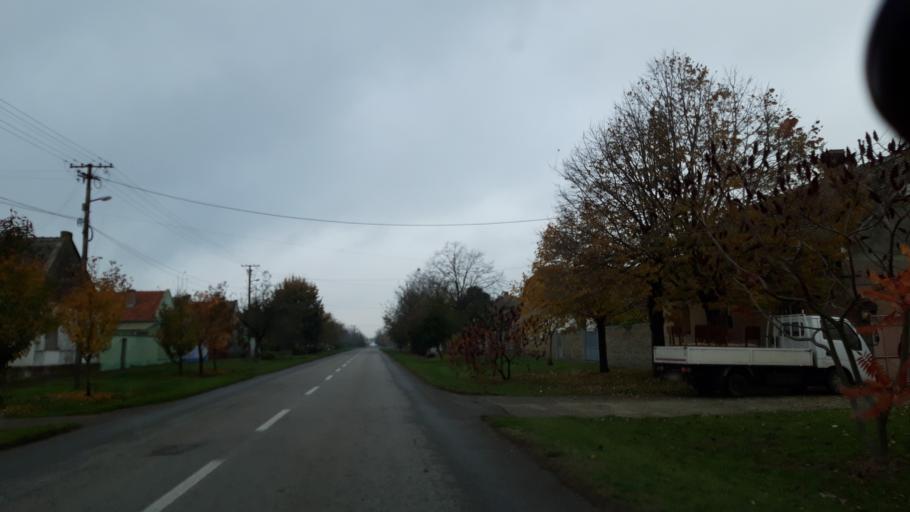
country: RS
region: Autonomna Pokrajina Vojvodina
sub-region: Juznobacki Okrug
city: Temerin
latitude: 45.5068
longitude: 19.9249
